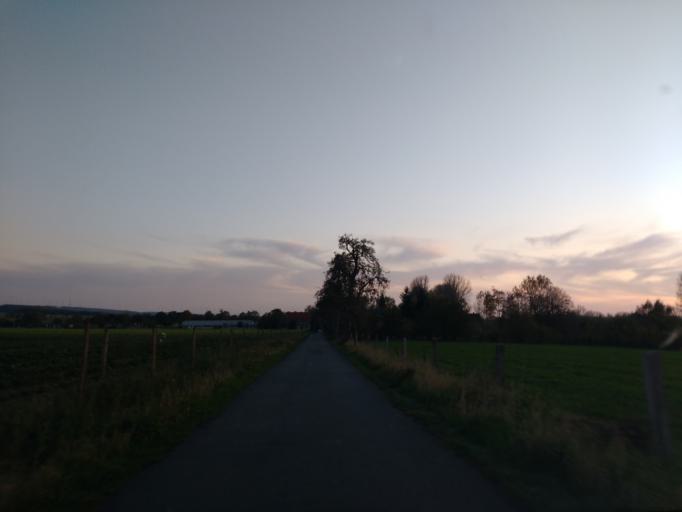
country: DE
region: North Rhine-Westphalia
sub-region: Regierungsbezirk Detmold
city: Schlangen
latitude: 51.8012
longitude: 8.8467
